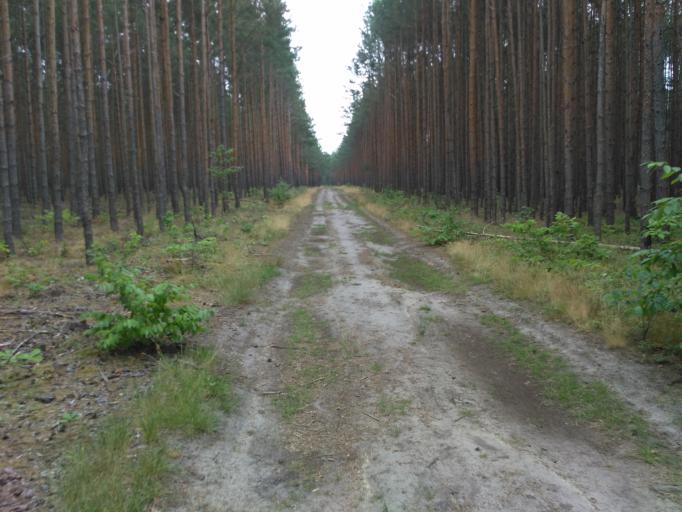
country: DE
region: Saxony
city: Hoyerswerda
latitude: 51.4555
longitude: 14.2785
